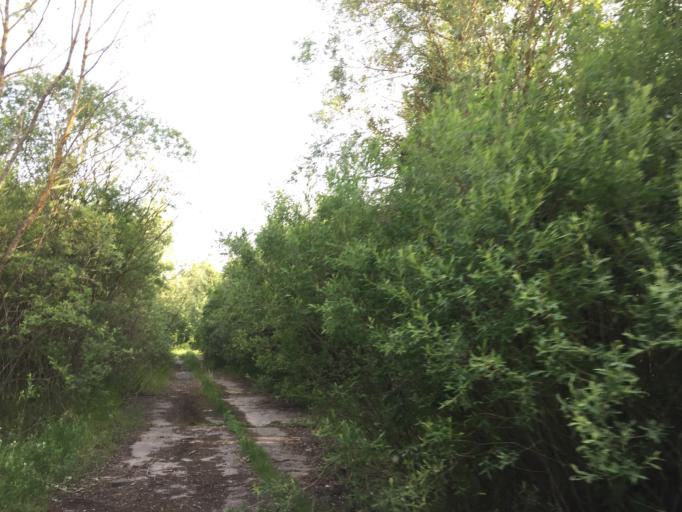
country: LV
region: Jelgava
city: Jelgava
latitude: 56.6709
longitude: 23.6674
